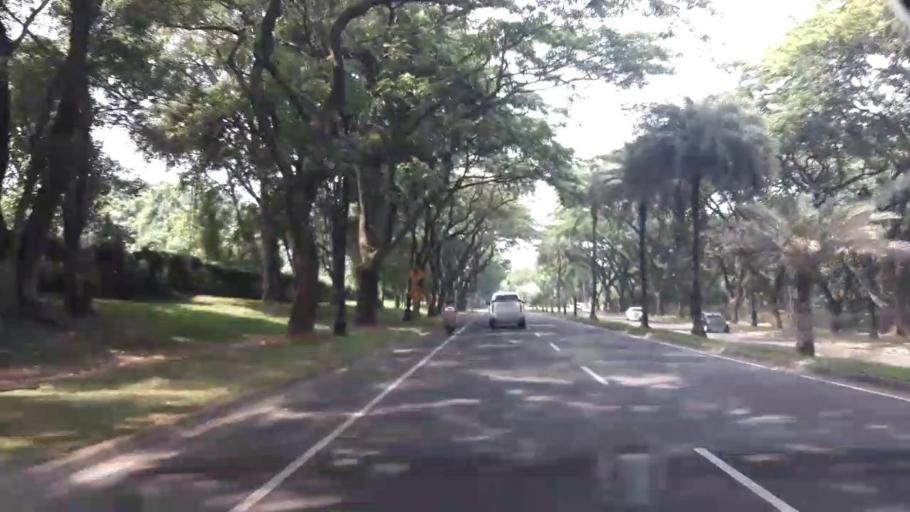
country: ID
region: Banten
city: Tangerang
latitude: -6.2317
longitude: 106.6084
